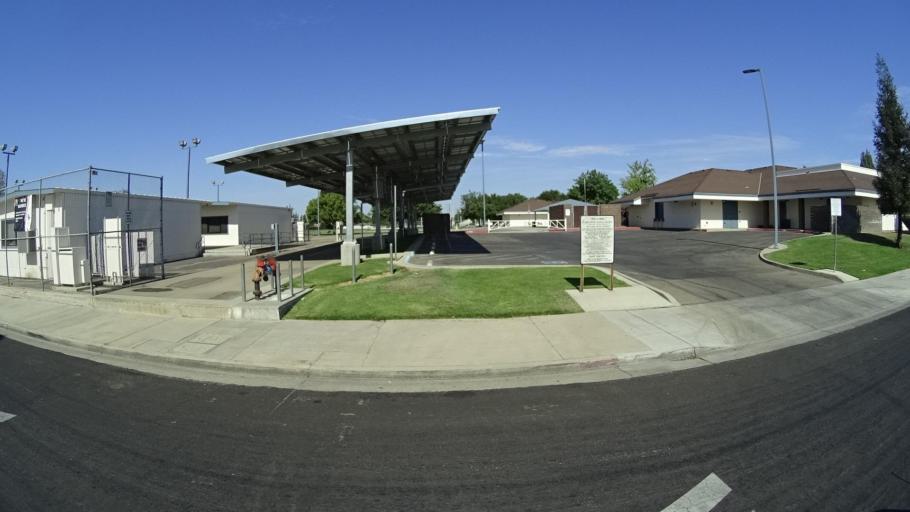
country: US
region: California
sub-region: Fresno County
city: Tarpey Village
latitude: 36.7901
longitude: -119.6862
